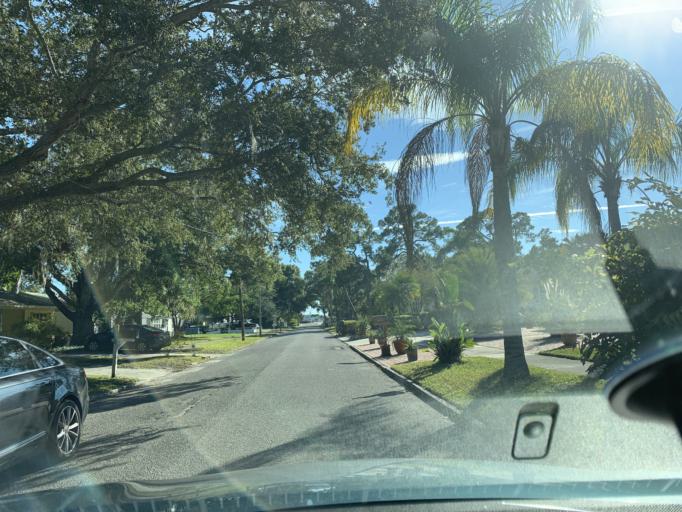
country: US
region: Florida
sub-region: Pinellas County
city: Gulfport
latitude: 27.7428
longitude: -82.6972
